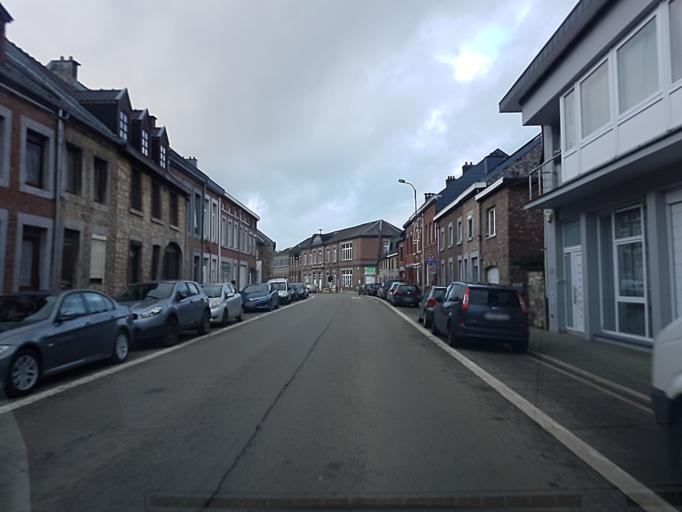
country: BE
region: Wallonia
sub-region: Province de Liege
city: Theux
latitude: 50.5440
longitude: 5.8126
